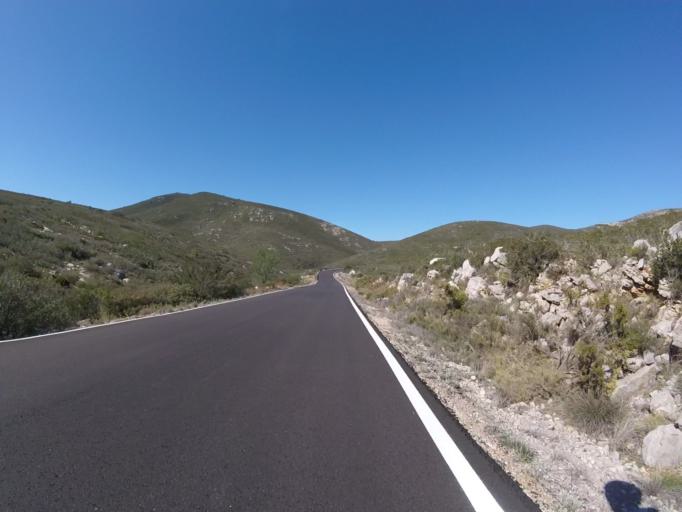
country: ES
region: Valencia
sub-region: Provincia de Castello
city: Cervera del Maestre
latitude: 40.4027
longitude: 0.2294
